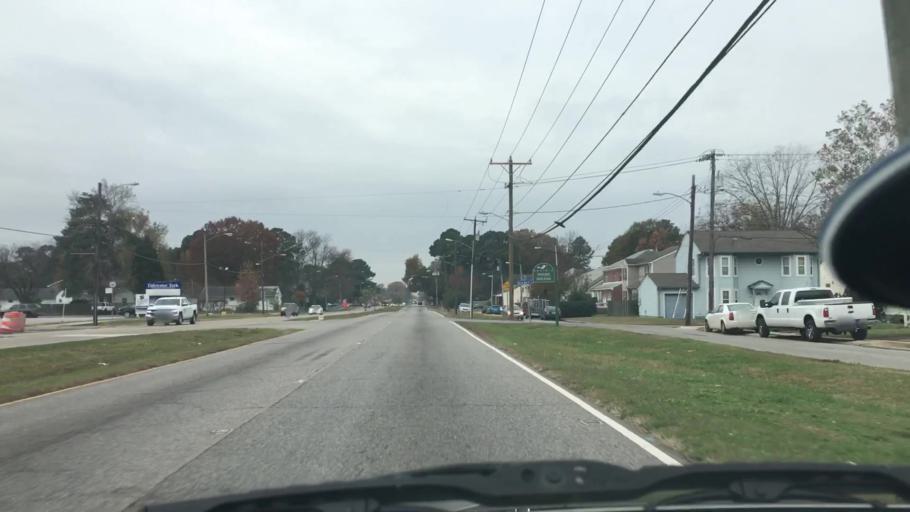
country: US
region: Virginia
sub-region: City of Norfolk
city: Norfolk
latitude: 36.8731
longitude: -76.2198
